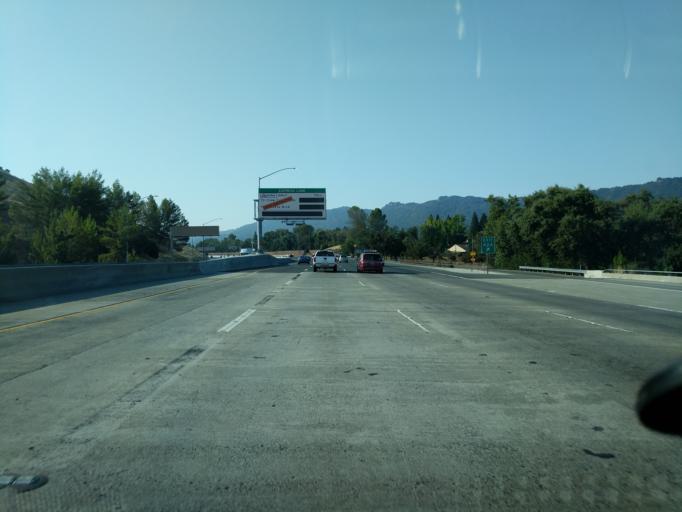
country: US
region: California
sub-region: Contra Costa County
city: Alamo
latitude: 37.8516
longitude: -122.0290
